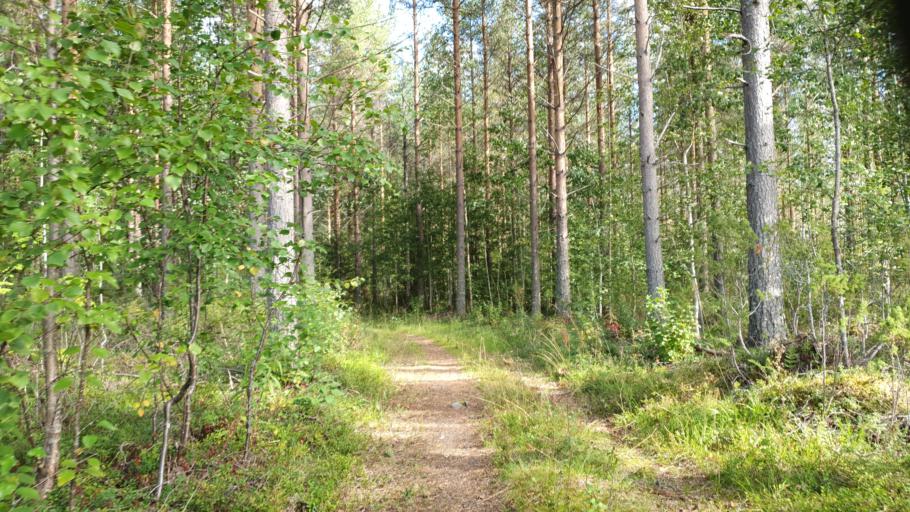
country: FI
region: Kainuu
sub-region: Kehys-Kainuu
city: Kuhmo
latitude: 64.1454
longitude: 29.3397
